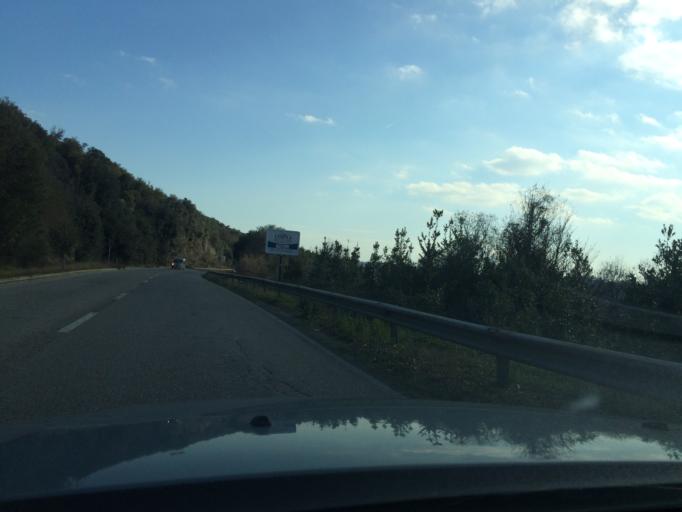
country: IT
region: Umbria
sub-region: Provincia di Terni
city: Amelia
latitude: 42.5575
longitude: 12.4397
